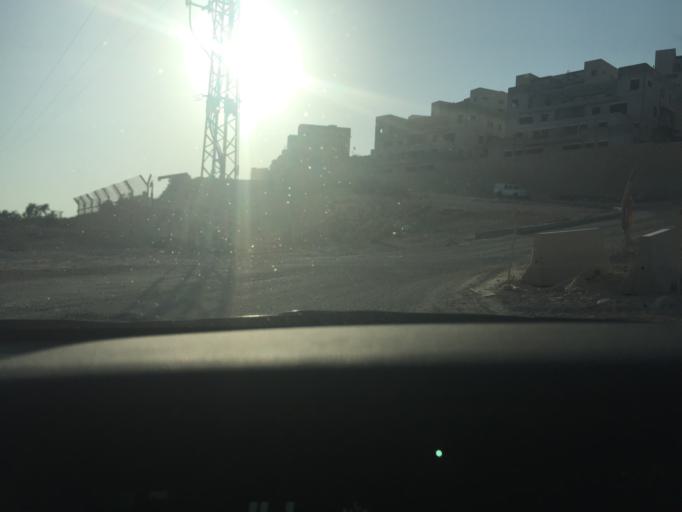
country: PS
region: West Bank
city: Rafat
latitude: 32.0660
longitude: 35.0500
